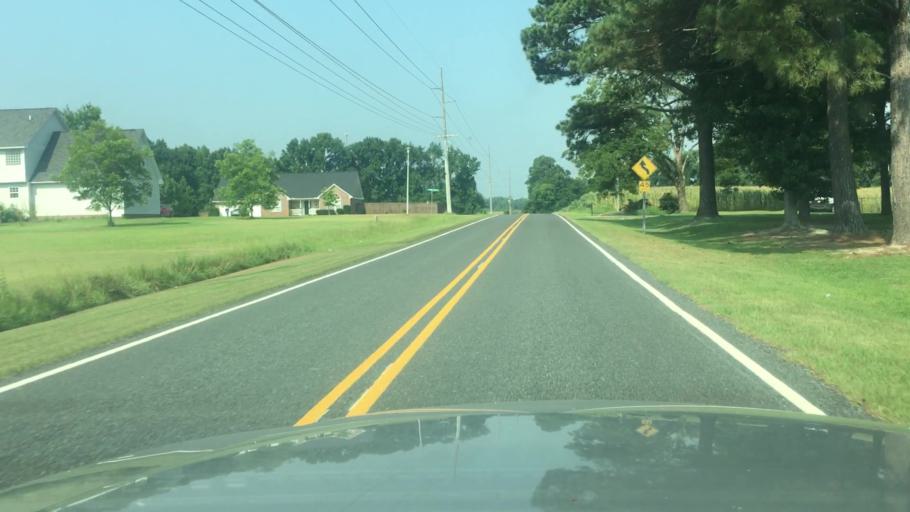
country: US
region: North Carolina
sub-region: Cumberland County
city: Hope Mills
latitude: 34.9002
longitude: -78.8806
